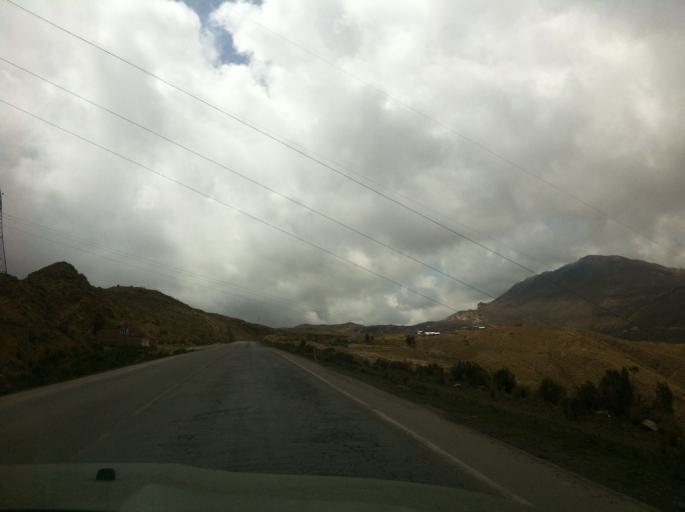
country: BO
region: Cochabamba
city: Irpa Irpa
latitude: -17.6745
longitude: -66.4849
